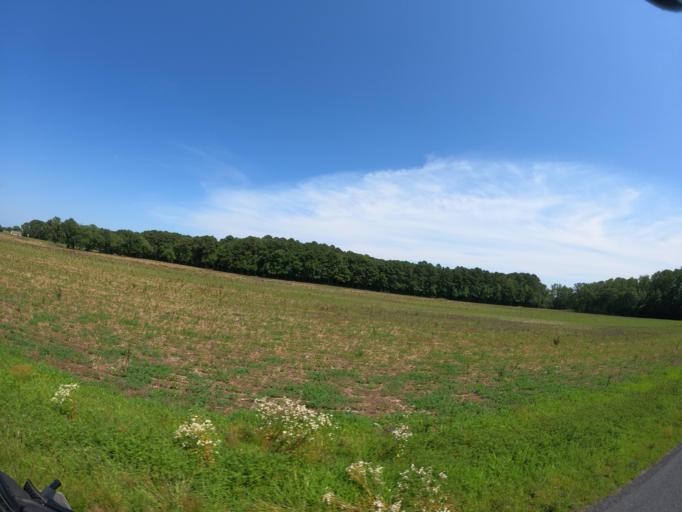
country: US
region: Maryland
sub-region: Worcester County
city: Ocean Pines
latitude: 38.4561
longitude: -75.1367
